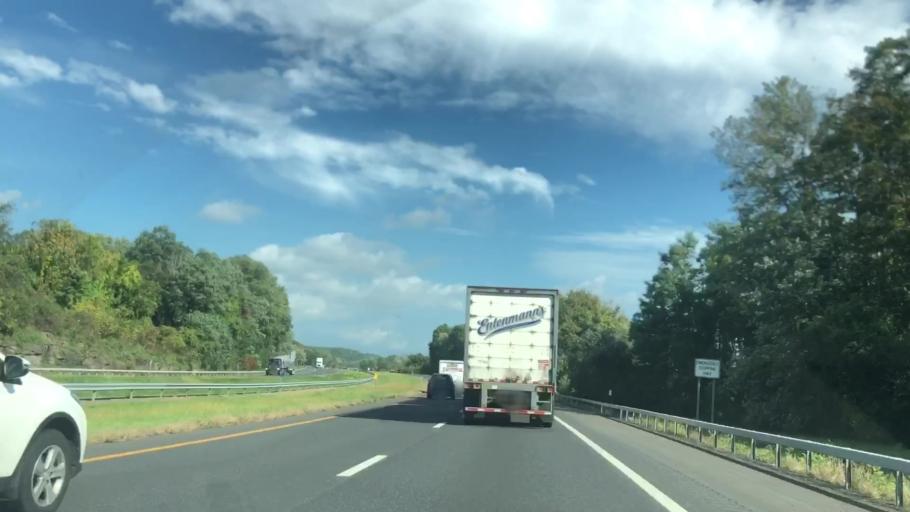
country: US
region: New York
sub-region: Ulster County
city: Lincoln Park
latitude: 41.9570
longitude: -74.0161
